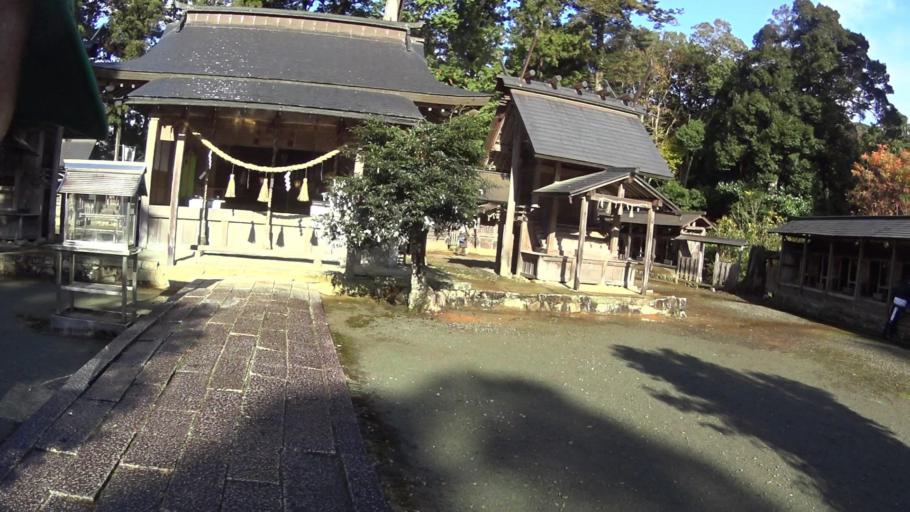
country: JP
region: Kyoto
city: Fukuchiyama
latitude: 35.4024
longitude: 135.1514
